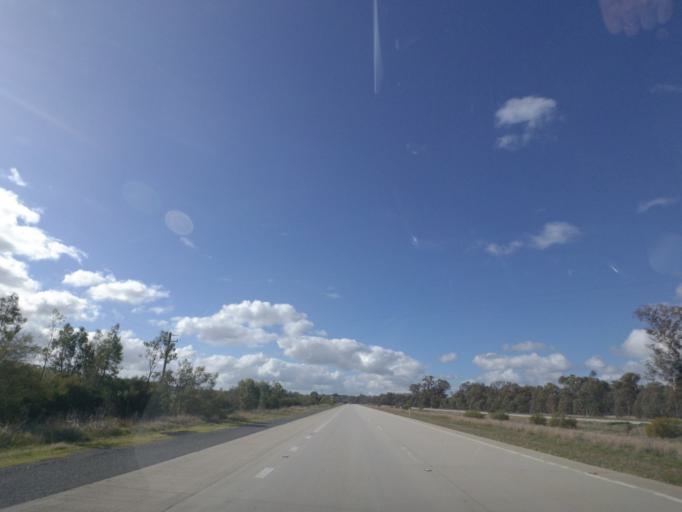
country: AU
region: New South Wales
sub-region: Greater Hume Shire
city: Holbrook
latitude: -35.9110
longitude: 147.1541
